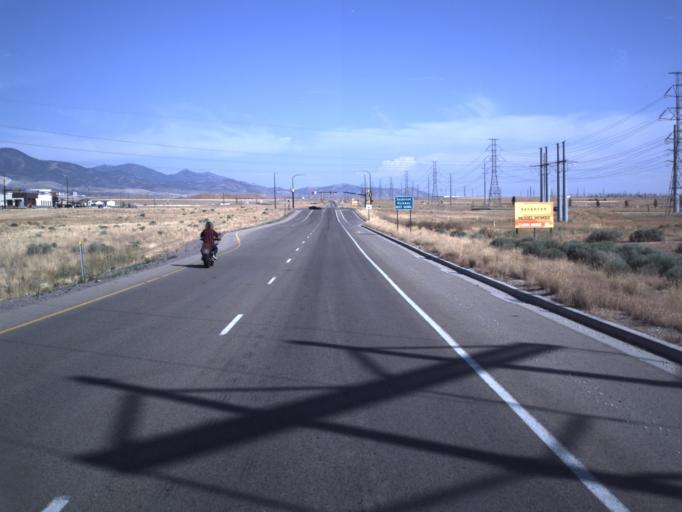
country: US
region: Utah
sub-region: Salt Lake County
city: Herriman
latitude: 40.5370
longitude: -112.0146
